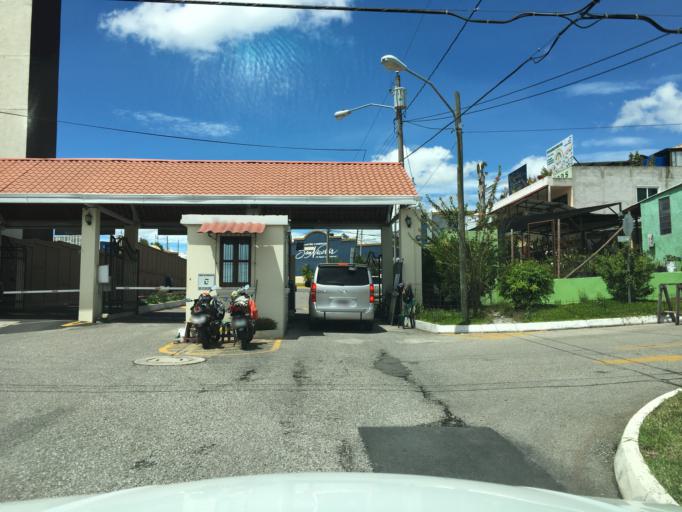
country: GT
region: Guatemala
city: Mixco
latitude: 14.6563
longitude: -90.5674
